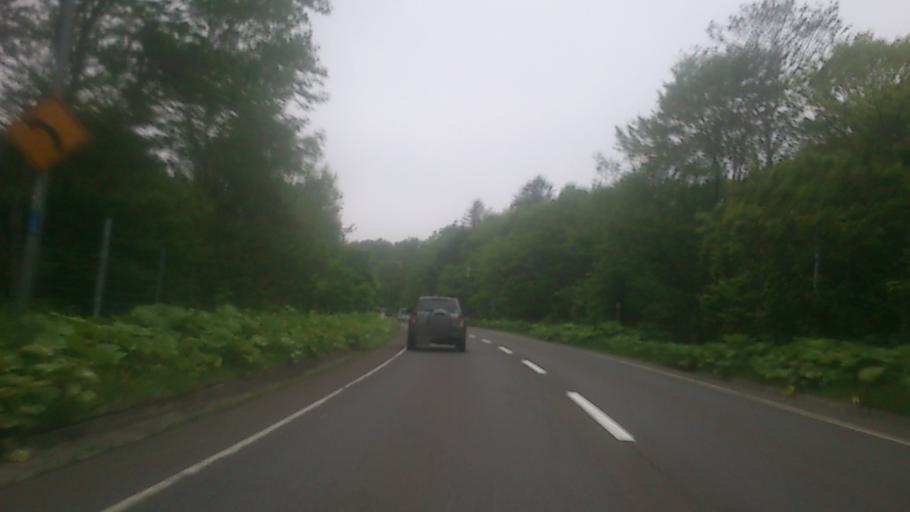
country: JP
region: Hokkaido
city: Kushiro
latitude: 42.9834
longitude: 144.5516
